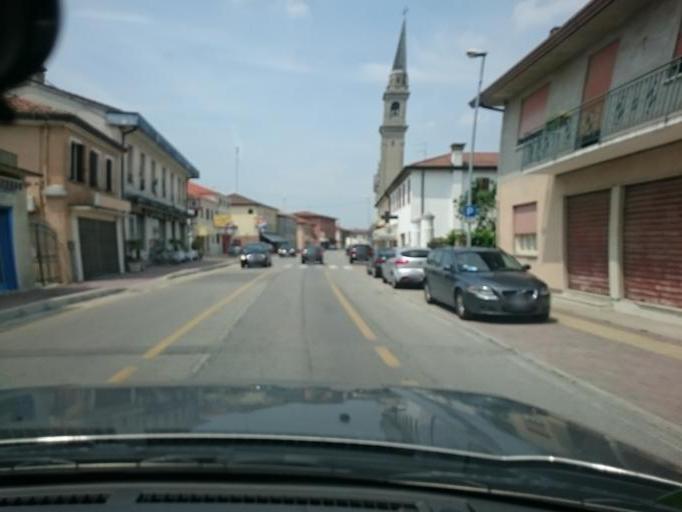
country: IT
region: Veneto
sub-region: Provincia di Padova
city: Campagnola
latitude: 45.2781
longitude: 11.9986
